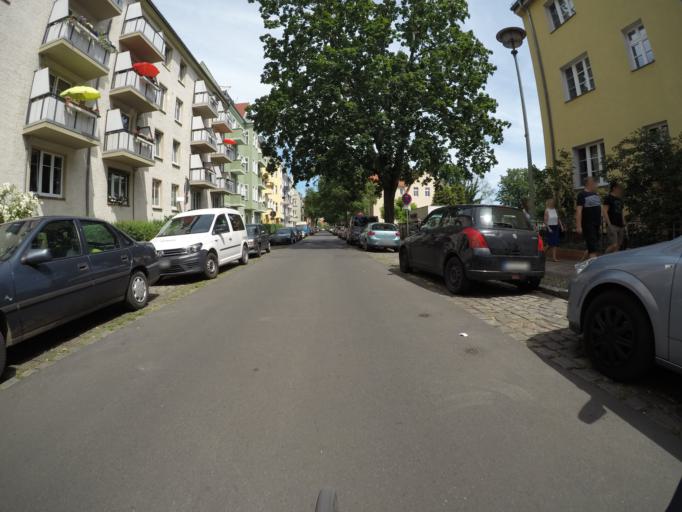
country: DE
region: Berlin
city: Kopenick Bezirk
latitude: 52.4458
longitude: 13.5700
